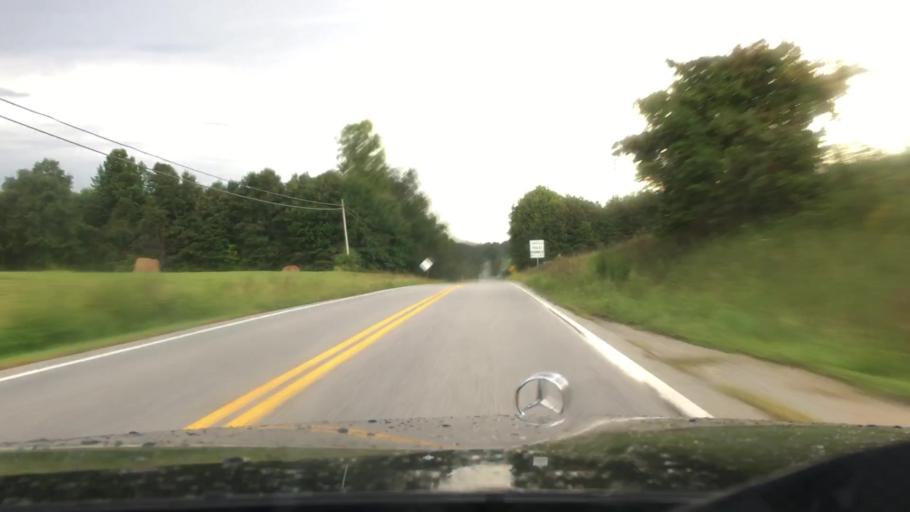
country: US
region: Virginia
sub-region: Nelson County
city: Lovingston
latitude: 37.7570
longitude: -78.9818
